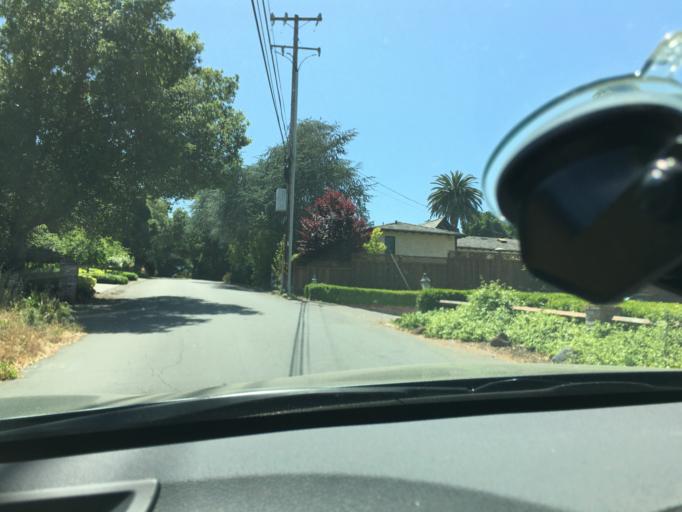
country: US
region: California
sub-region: Santa Clara County
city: Loyola
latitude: 37.3521
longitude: -122.0923
